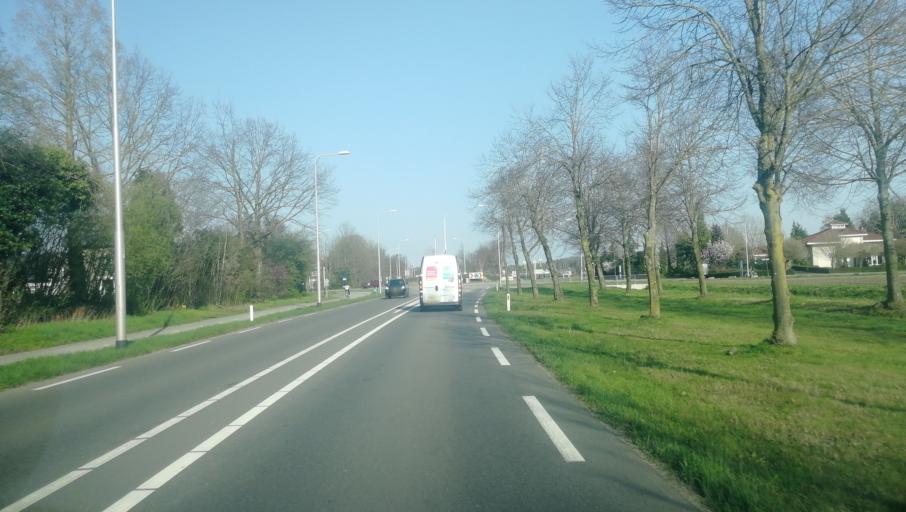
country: NL
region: Limburg
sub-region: Gemeente Peel en Maas
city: Maasbree
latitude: 51.3546
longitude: 6.0438
